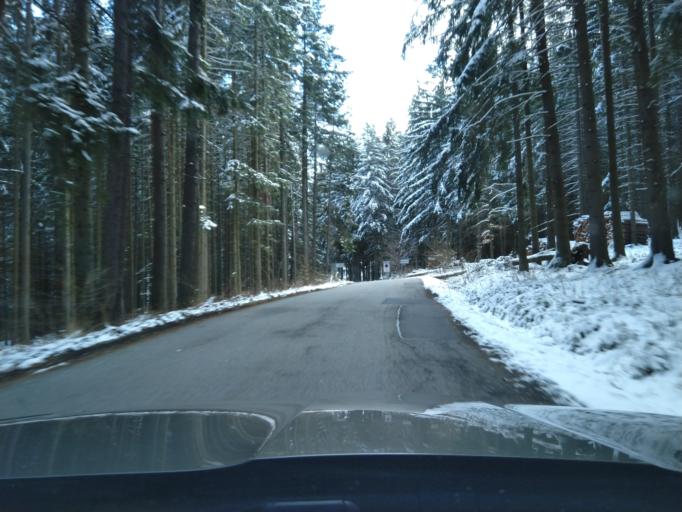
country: CZ
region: Jihocesky
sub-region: Okres Prachatice
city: Vimperk
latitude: 49.0583
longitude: 13.7571
